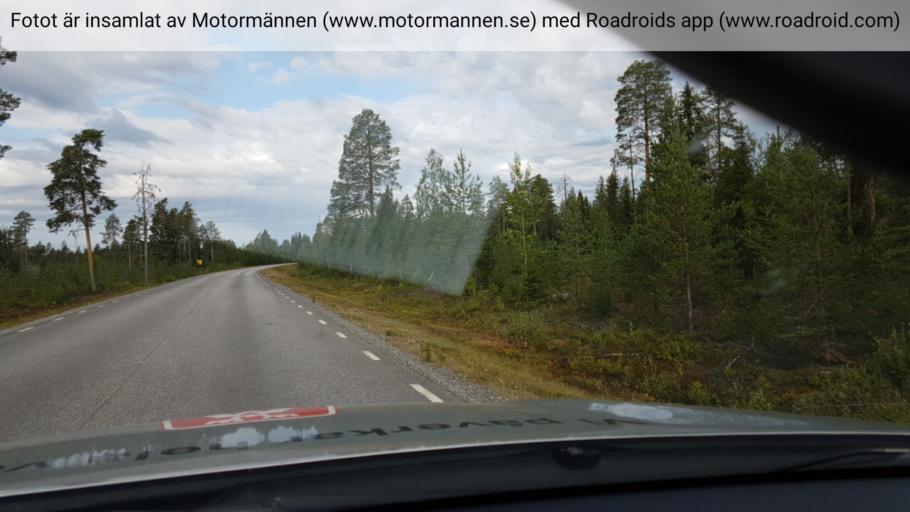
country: SE
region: Vaesterbotten
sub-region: Skelleftea Kommun
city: Storvik
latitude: 65.3758
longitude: 20.3637
